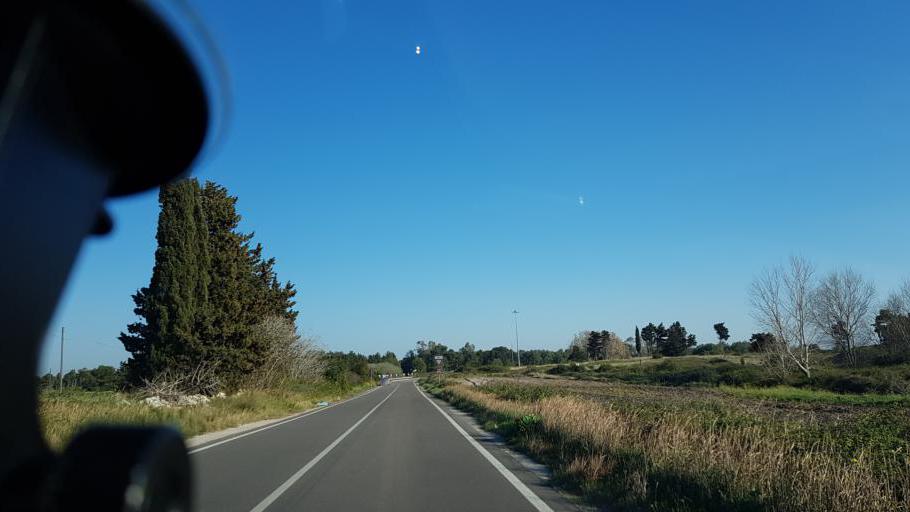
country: IT
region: Apulia
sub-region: Provincia di Lecce
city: Merine
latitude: 40.4113
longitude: 18.2560
